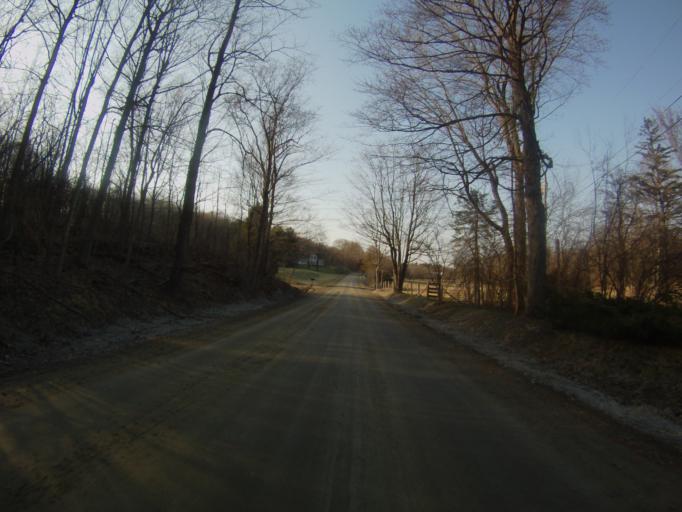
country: US
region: Vermont
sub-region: Addison County
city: Middlebury (village)
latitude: 44.0365
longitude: -73.1454
